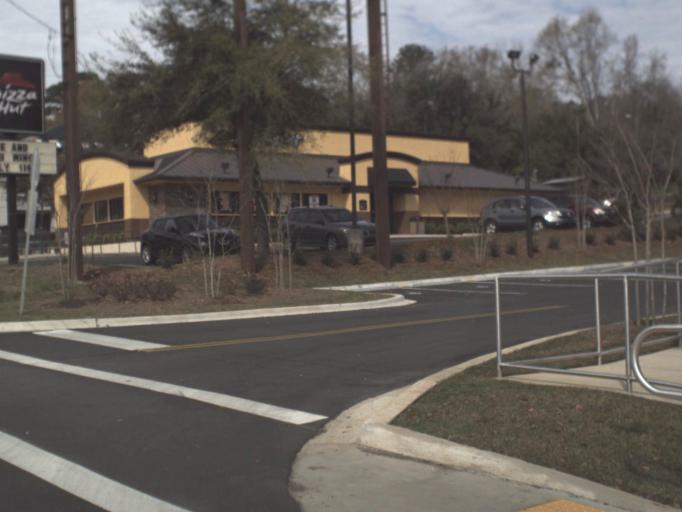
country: US
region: Florida
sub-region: Leon County
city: Tallahassee
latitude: 30.4492
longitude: -84.3103
